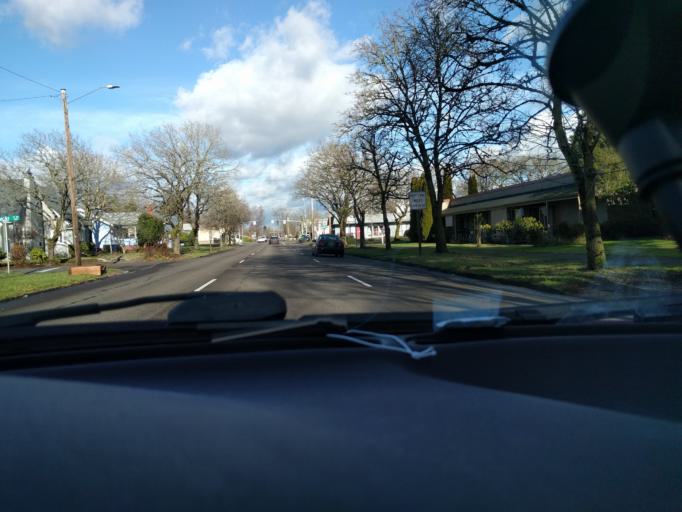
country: US
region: Oregon
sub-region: Marion County
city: Salem
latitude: 44.9480
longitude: -123.0238
